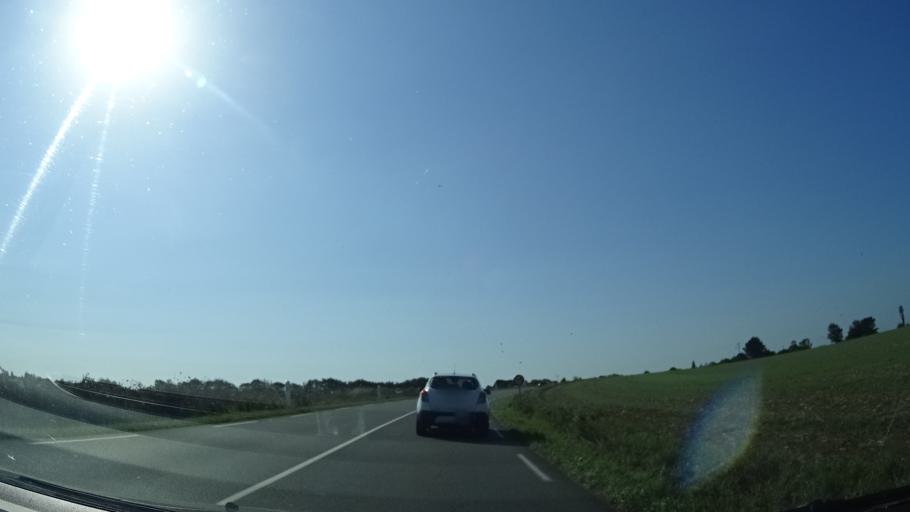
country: FR
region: Brittany
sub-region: Departement du Finistere
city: Plonevez-Porzay
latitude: 48.1066
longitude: -4.2455
